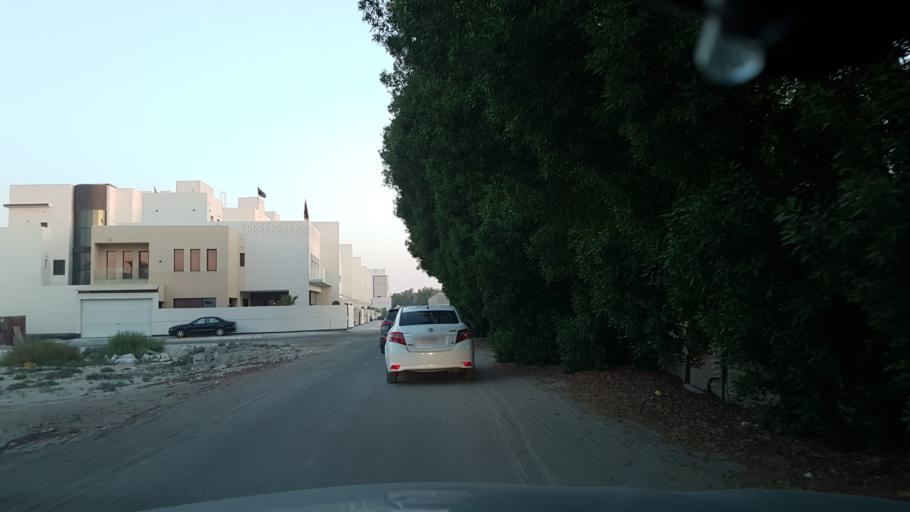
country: BH
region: Manama
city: Jidd Hafs
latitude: 26.2342
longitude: 50.5057
